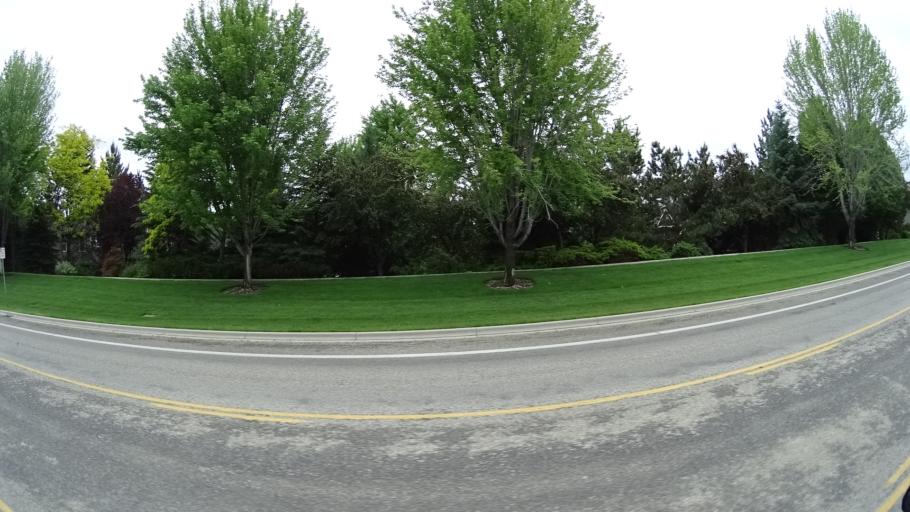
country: US
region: Idaho
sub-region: Ada County
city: Eagle
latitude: 43.7064
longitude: -116.3497
